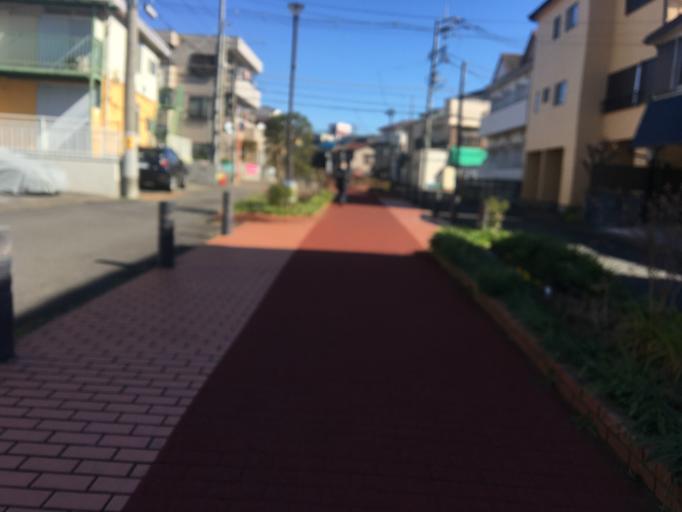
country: JP
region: Saitama
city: Shiki
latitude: 35.8312
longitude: 139.5671
